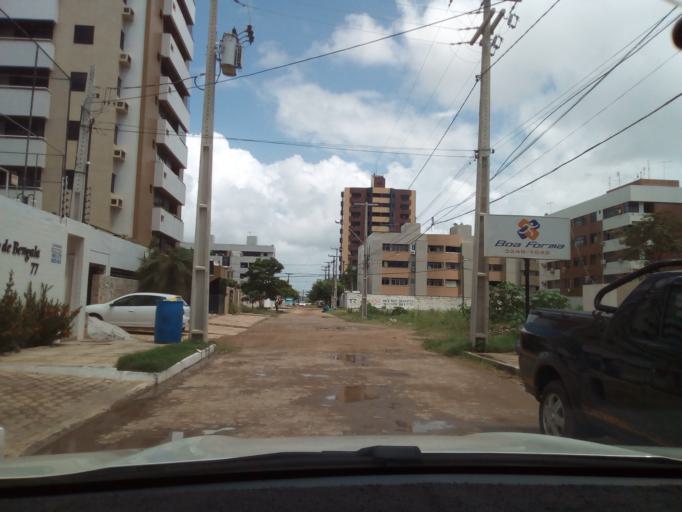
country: BR
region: Paraiba
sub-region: Cabedelo
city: Cabedelo
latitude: -7.0404
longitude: -34.8410
